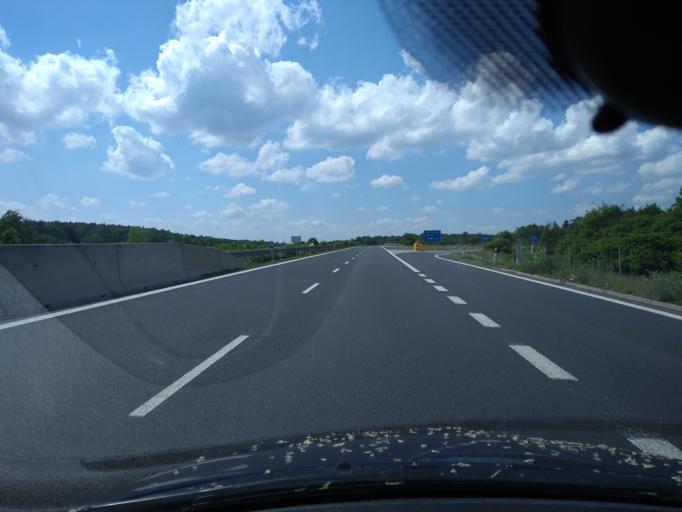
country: CZ
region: Plzensky
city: Chlumcany
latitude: 49.6623
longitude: 13.3452
